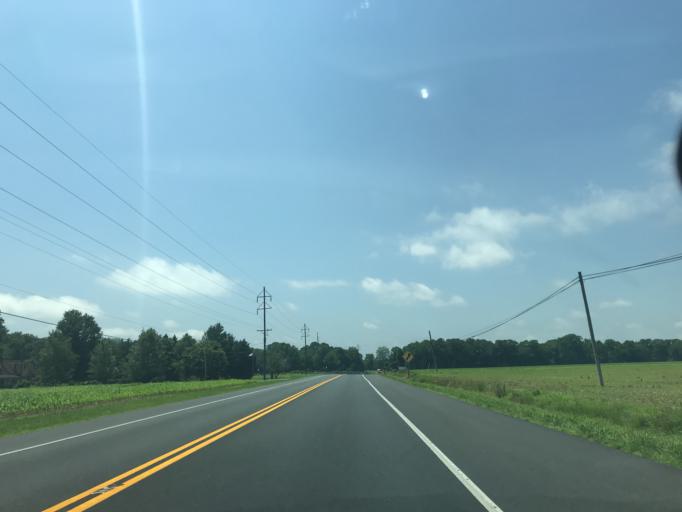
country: US
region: Maryland
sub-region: Dorchester County
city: Hurlock
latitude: 38.5917
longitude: -75.9388
